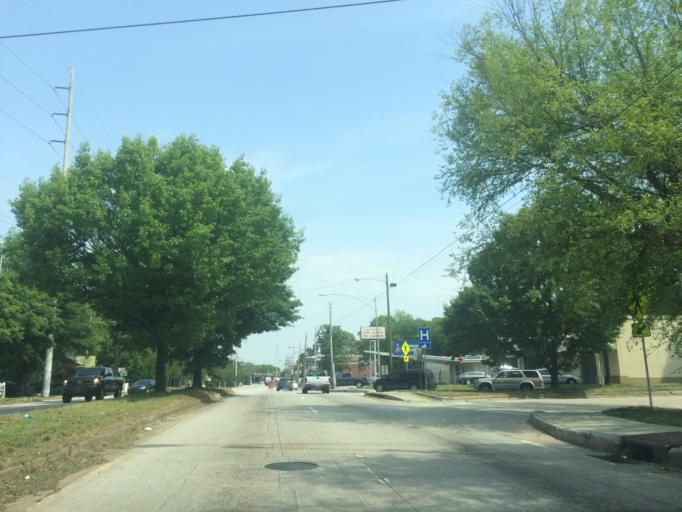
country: US
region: Georgia
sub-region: DeKalb County
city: Druid Hills
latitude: 33.7615
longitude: -84.3492
